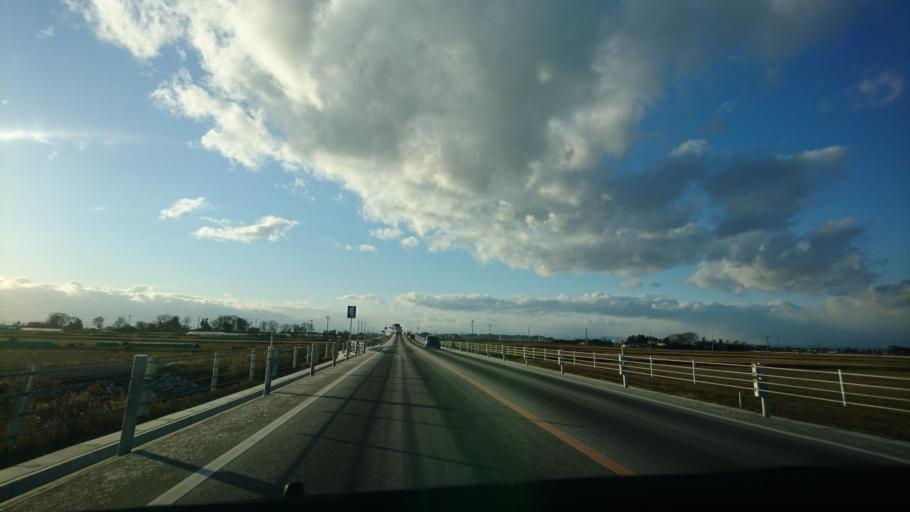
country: JP
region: Miyagi
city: Wakuya
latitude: 38.6856
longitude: 141.2420
